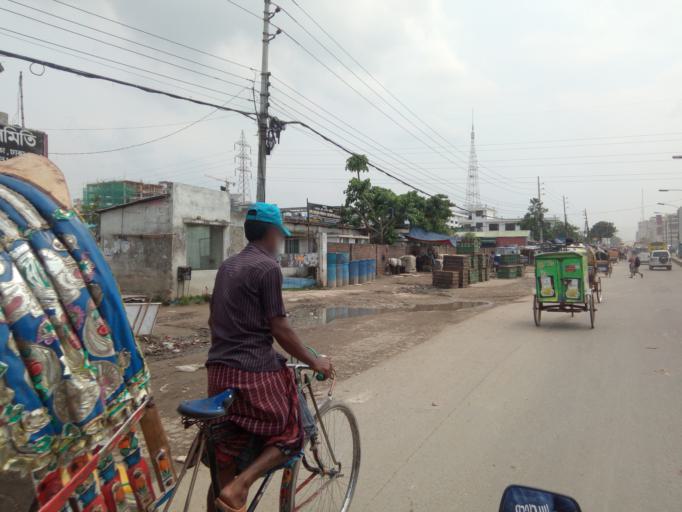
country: BD
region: Dhaka
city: Paltan
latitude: 23.7697
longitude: 90.4242
